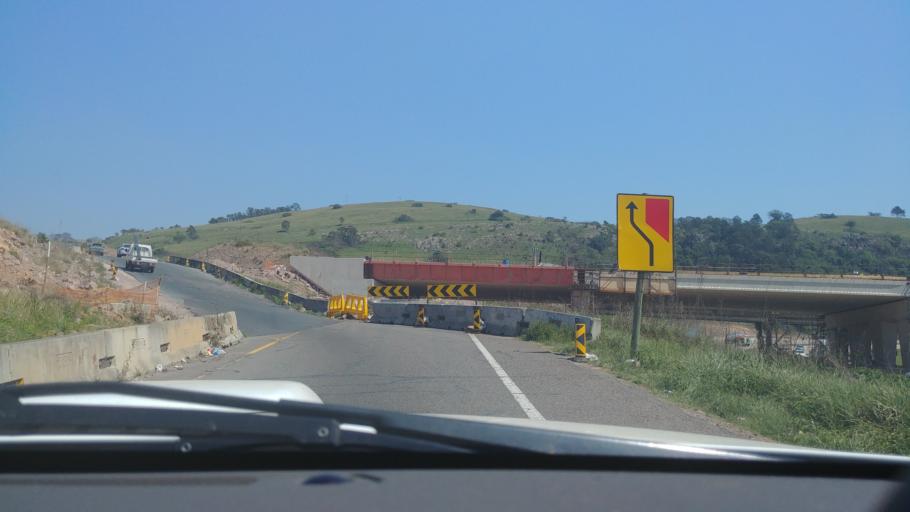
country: ZA
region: KwaZulu-Natal
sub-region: eThekwini Metropolitan Municipality
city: Mpumalanga
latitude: -29.7587
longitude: 30.6673
